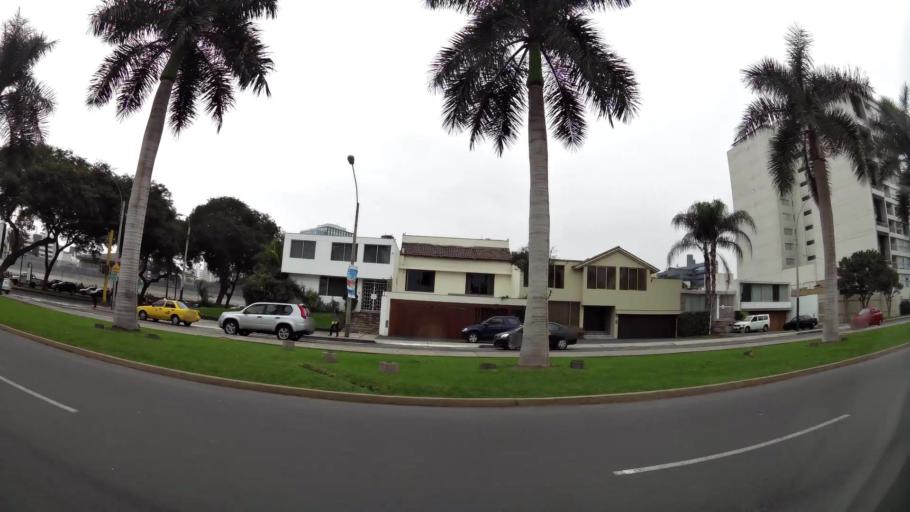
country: PE
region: Lima
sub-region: Lima
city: San Isidro
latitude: -12.0953
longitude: -77.0538
